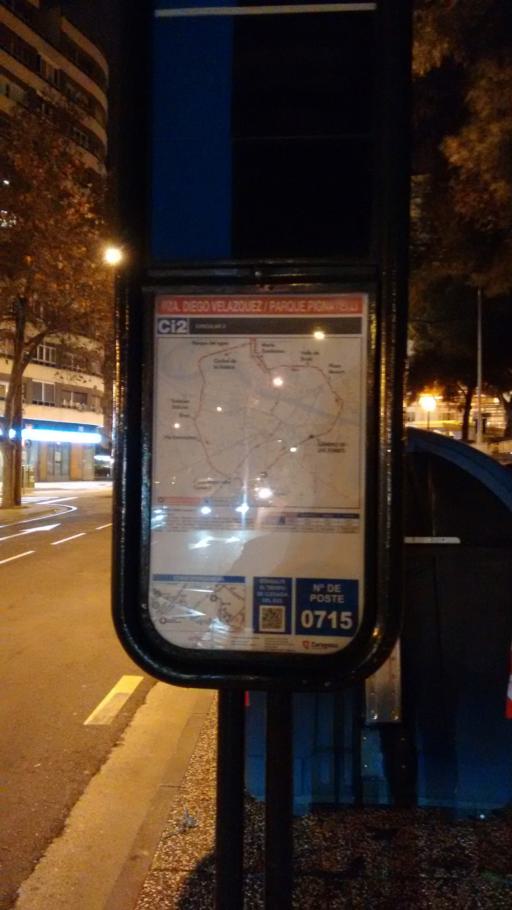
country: ES
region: Aragon
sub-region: Provincia de Zaragoza
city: Zaragoza
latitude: 41.6385
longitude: -0.8865
